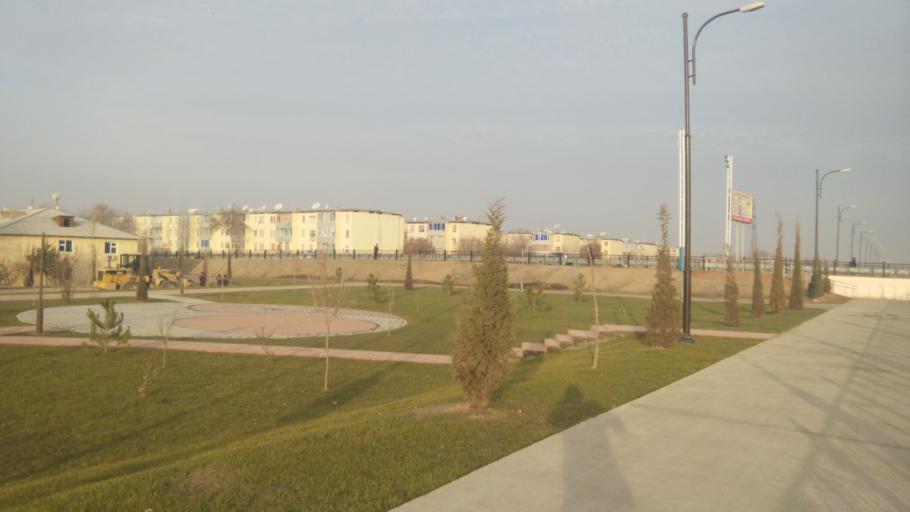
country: UZ
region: Sirdaryo
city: Guliston
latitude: 40.5105
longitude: 68.7773
